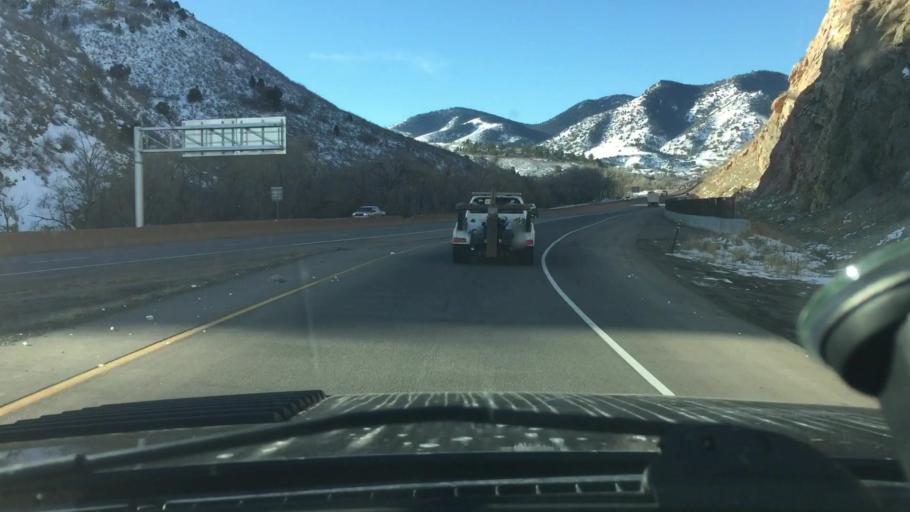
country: US
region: Colorado
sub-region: Jefferson County
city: Indian Hills
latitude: 39.6353
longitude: -105.1697
